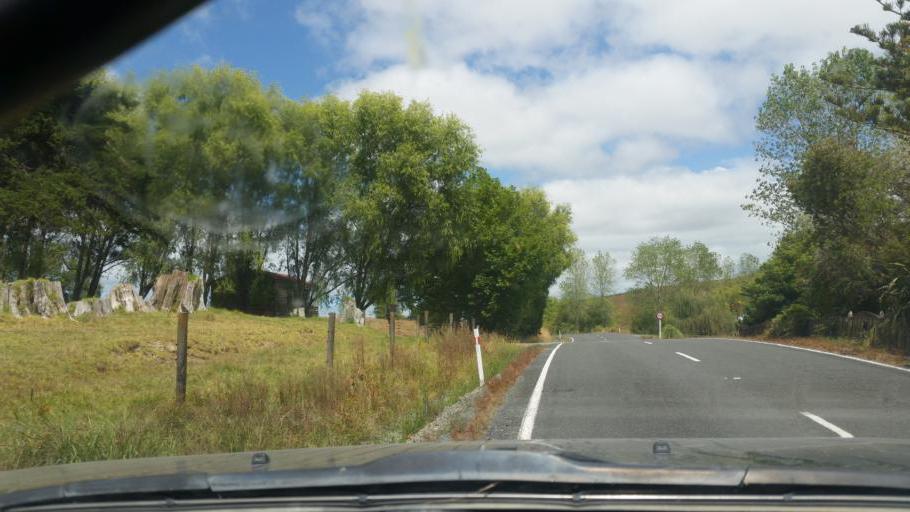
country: NZ
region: Auckland
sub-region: Auckland
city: Wellsford
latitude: -36.1243
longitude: 174.3304
